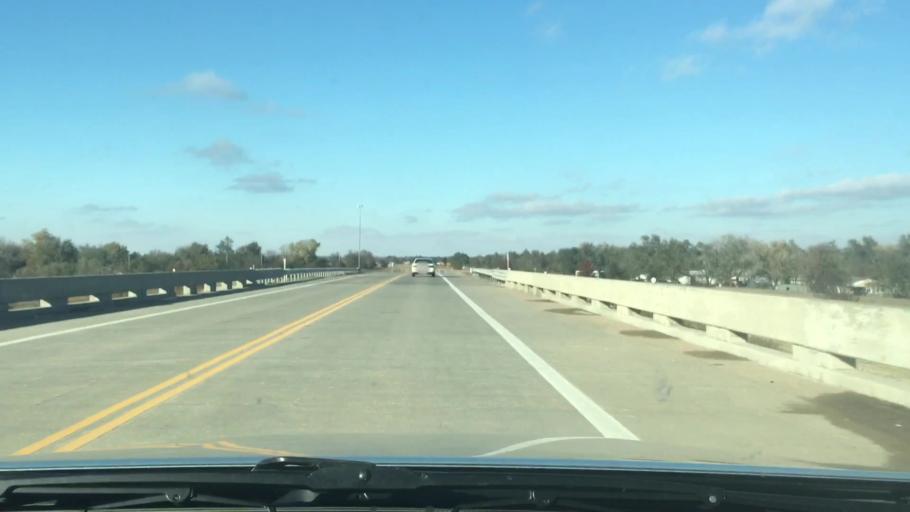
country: US
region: Kansas
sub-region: Reno County
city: South Hutchinson
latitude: 38.0574
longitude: -97.9859
